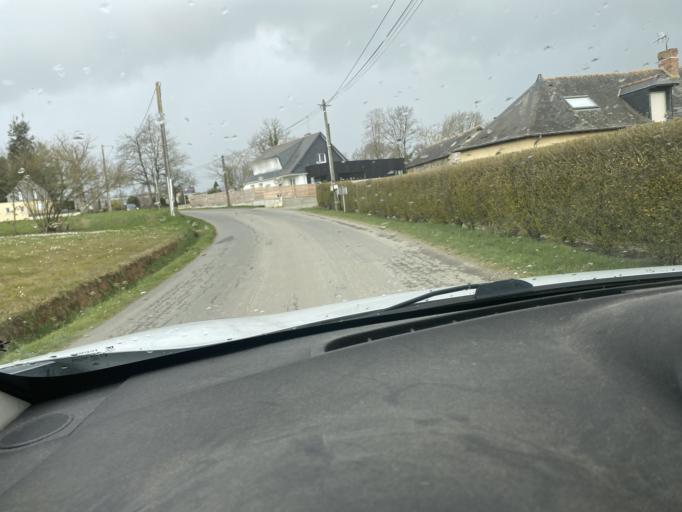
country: FR
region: Brittany
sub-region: Departement d'Ille-et-Vilaine
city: La Chapelle-des-Fougeretz
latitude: 48.1878
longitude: -1.7035
